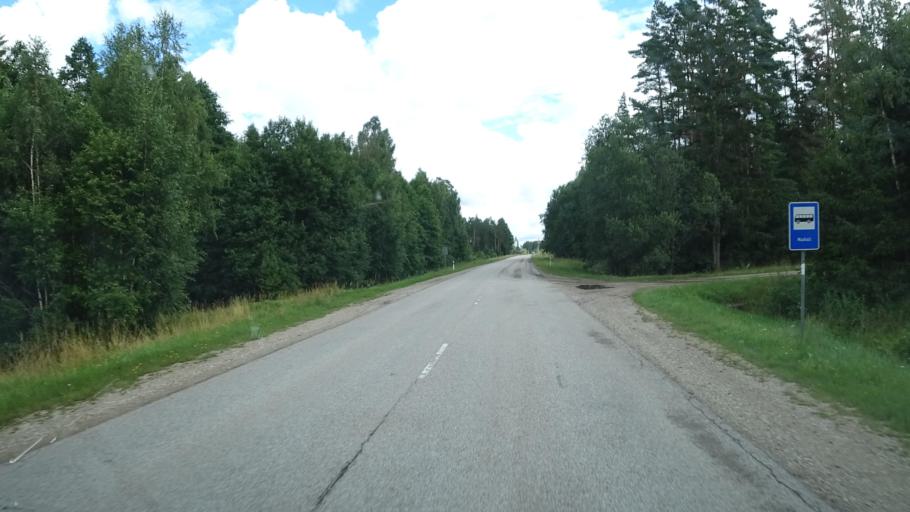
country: LV
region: Pavilostas
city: Pavilosta
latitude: 56.7431
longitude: 21.2374
